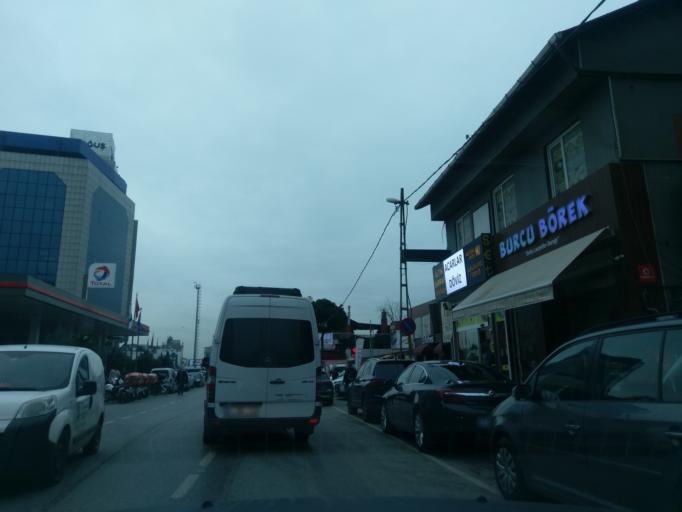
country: TR
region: Istanbul
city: Umraniye
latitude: 41.0950
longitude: 29.0980
